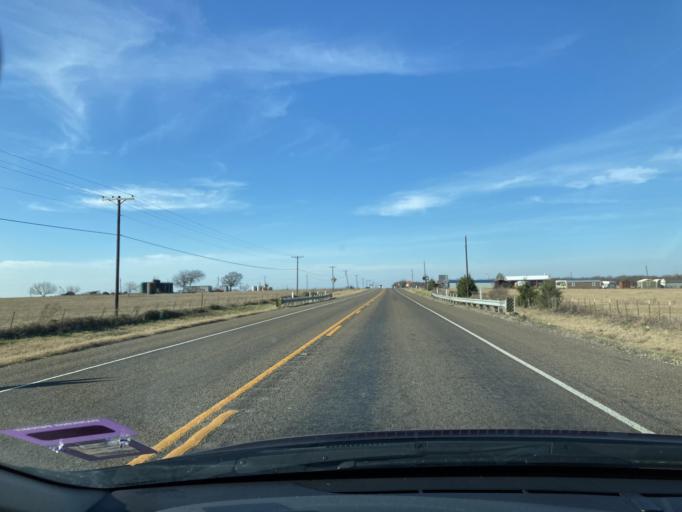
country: US
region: Texas
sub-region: Navarro County
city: Corsicana
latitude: 32.0389
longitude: -96.4069
